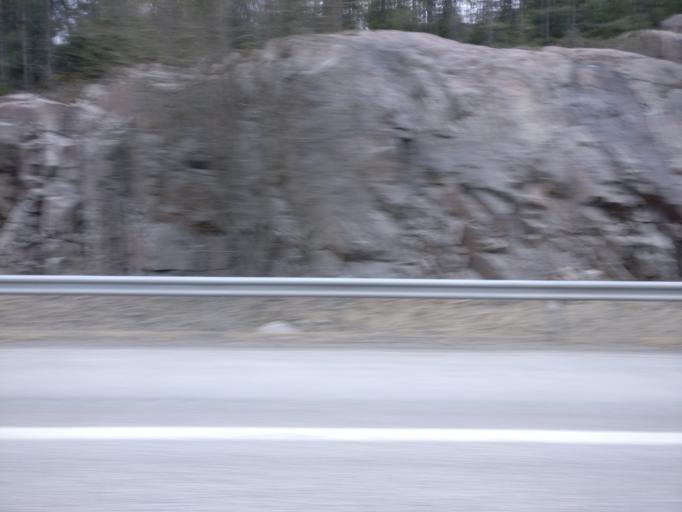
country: FI
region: Haeme
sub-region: Riihimaeki
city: Riihimaeki
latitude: 60.6669
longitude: 24.7850
